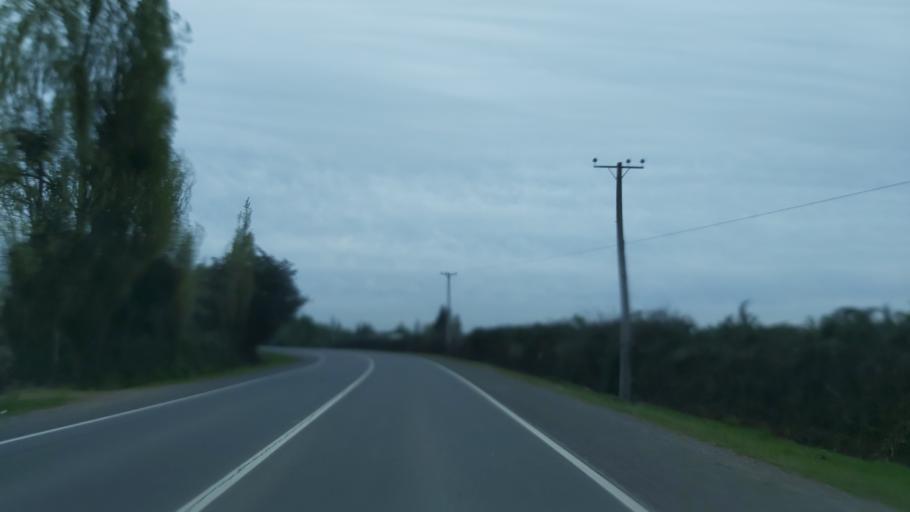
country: CL
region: Maule
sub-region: Provincia de Linares
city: Linares
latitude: -35.7657
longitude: -71.5124
